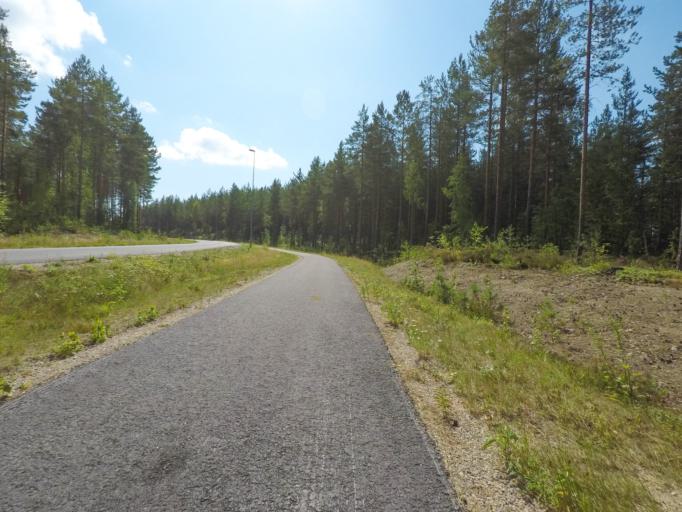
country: FI
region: Southern Savonia
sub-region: Mikkeli
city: Puumala
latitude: 61.5108
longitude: 28.1652
